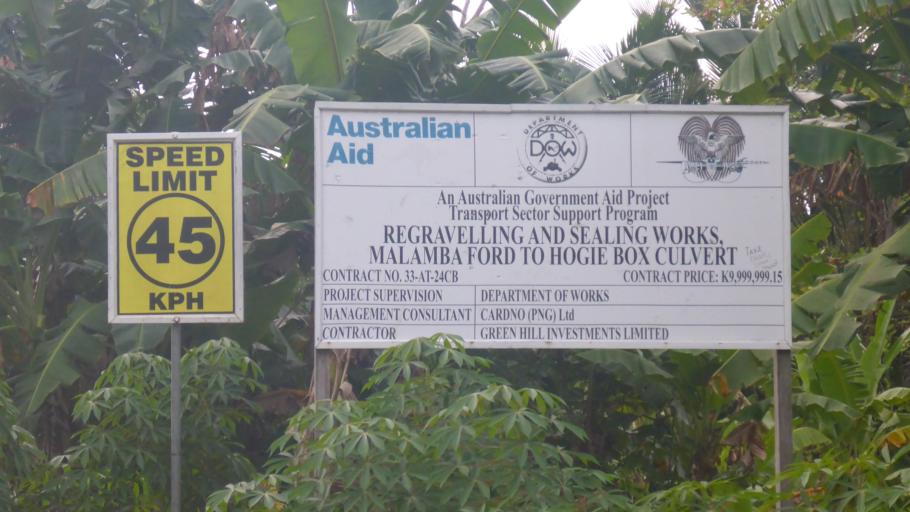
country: PG
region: East Sepik
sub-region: Wewak
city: Wewak
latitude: -3.4229
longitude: 143.4476
